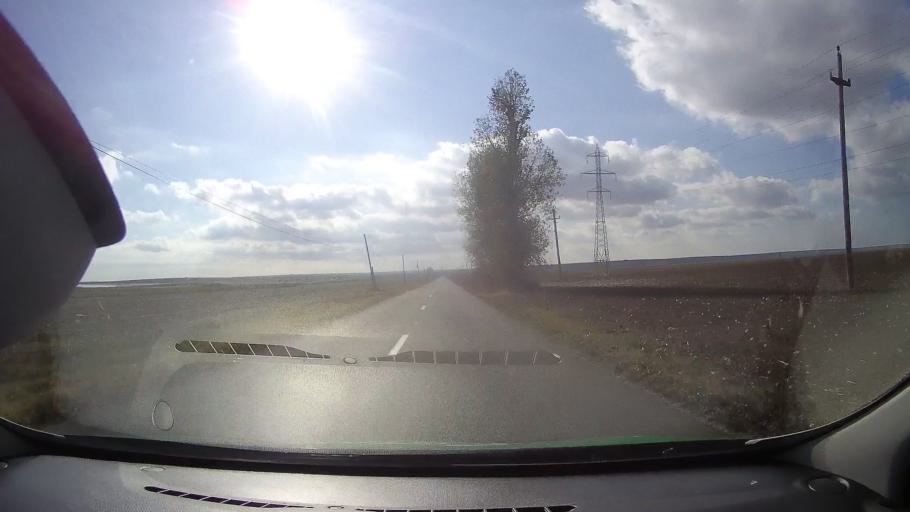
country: RO
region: Constanta
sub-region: Comuna Istria
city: Istria
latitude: 44.5420
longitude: 28.6903
